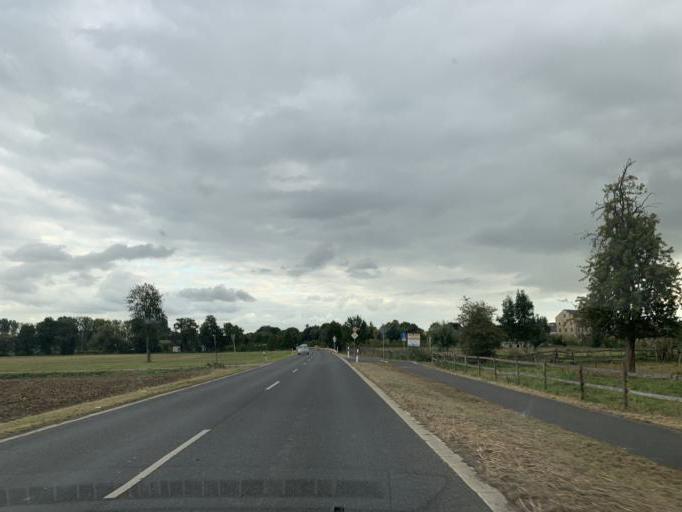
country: DE
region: North Rhine-Westphalia
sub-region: Regierungsbezirk Koln
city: Linnich
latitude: 51.0063
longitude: 6.2452
